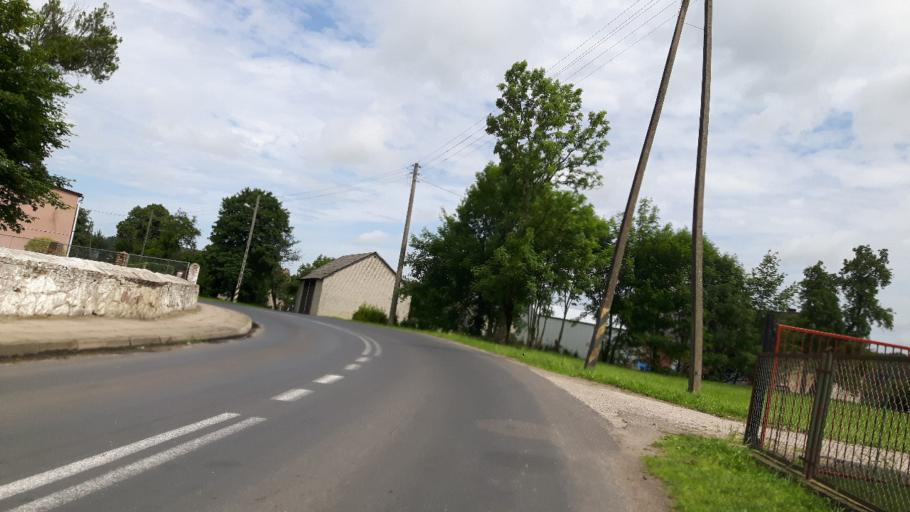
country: PL
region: West Pomeranian Voivodeship
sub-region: Powiat gryficki
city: Trzebiatow
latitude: 54.0120
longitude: 15.2459
